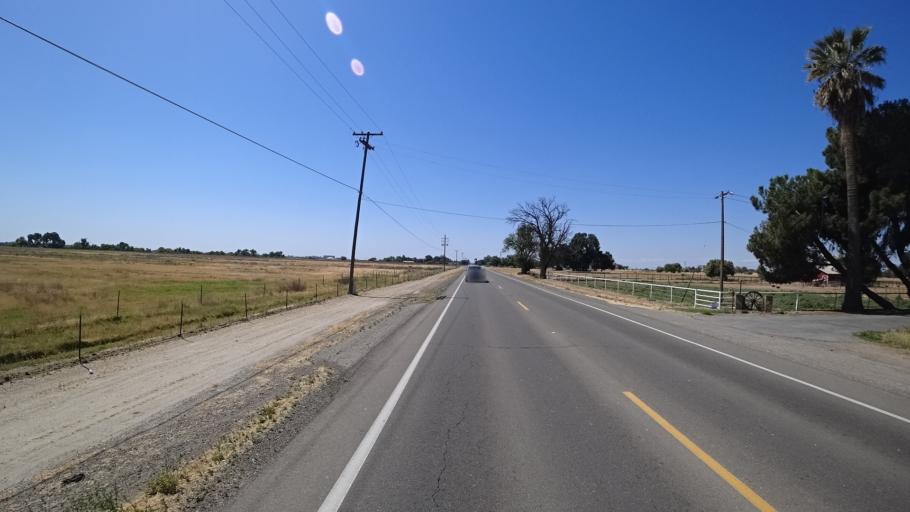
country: US
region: California
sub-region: Kings County
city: Lemoore
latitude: 36.2645
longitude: -119.7809
